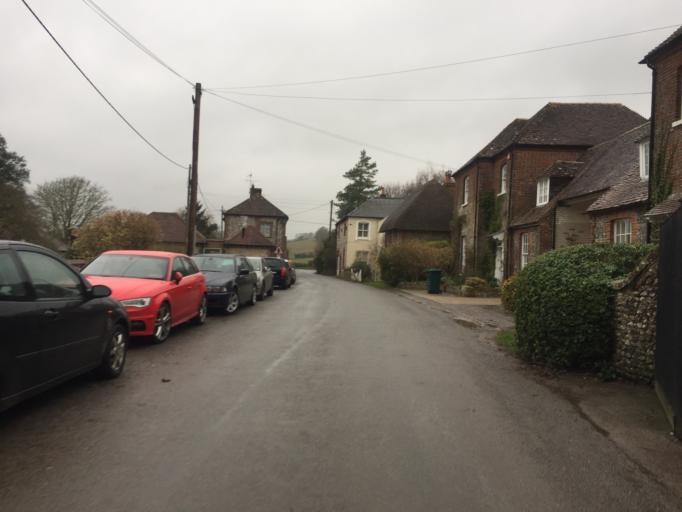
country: GB
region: England
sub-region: West Sussex
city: Boxgrove
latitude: 50.9098
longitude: -0.7376
